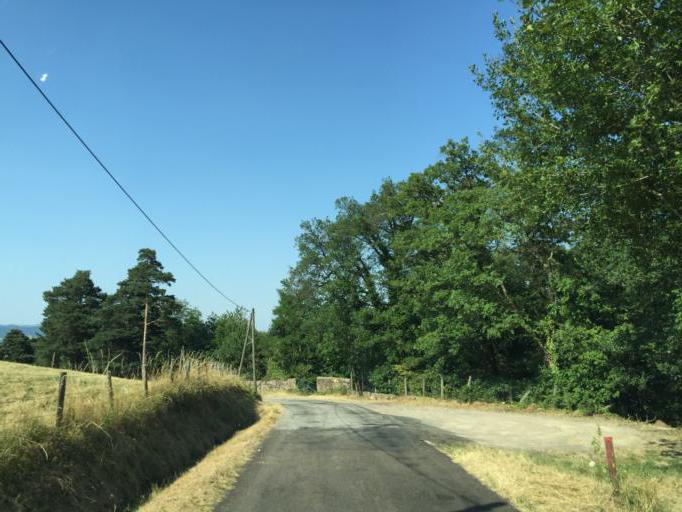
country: FR
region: Rhone-Alpes
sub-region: Departement de la Loire
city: Saint-Chamond
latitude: 45.4402
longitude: 4.5037
